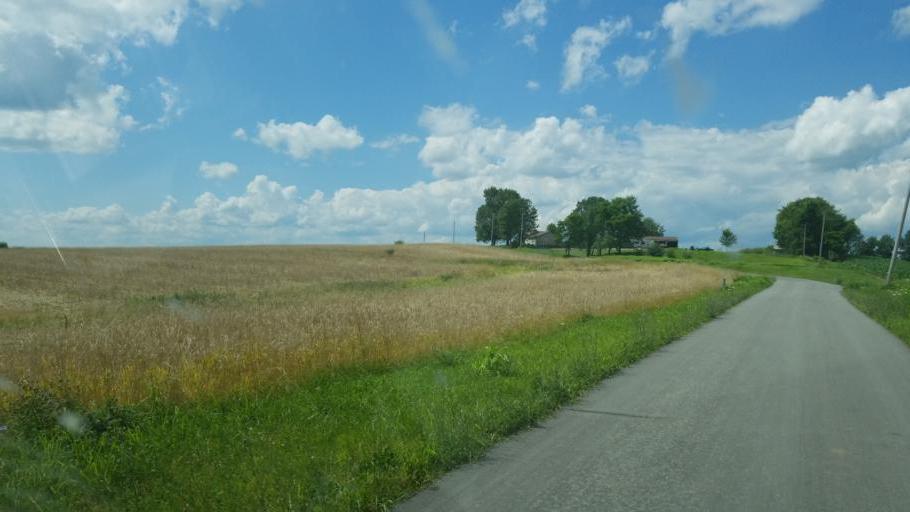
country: US
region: Ohio
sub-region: Highland County
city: Greenfield
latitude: 39.2529
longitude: -83.4288
